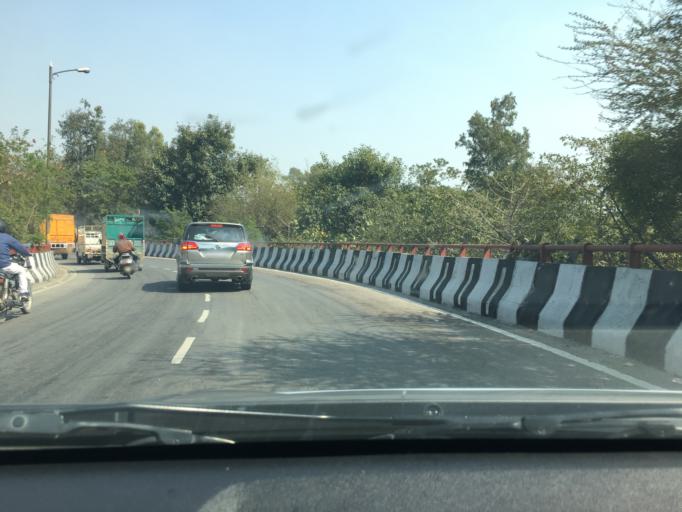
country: IN
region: NCT
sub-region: North Delhi
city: Delhi
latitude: 28.6499
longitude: 77.2507
